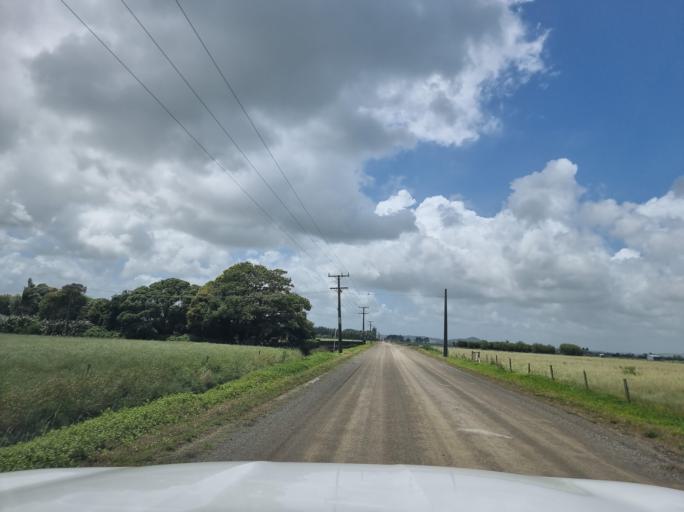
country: NZ
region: Northland
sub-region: Kaipara District
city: Dargaville
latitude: -36.0864
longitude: 173.9980
